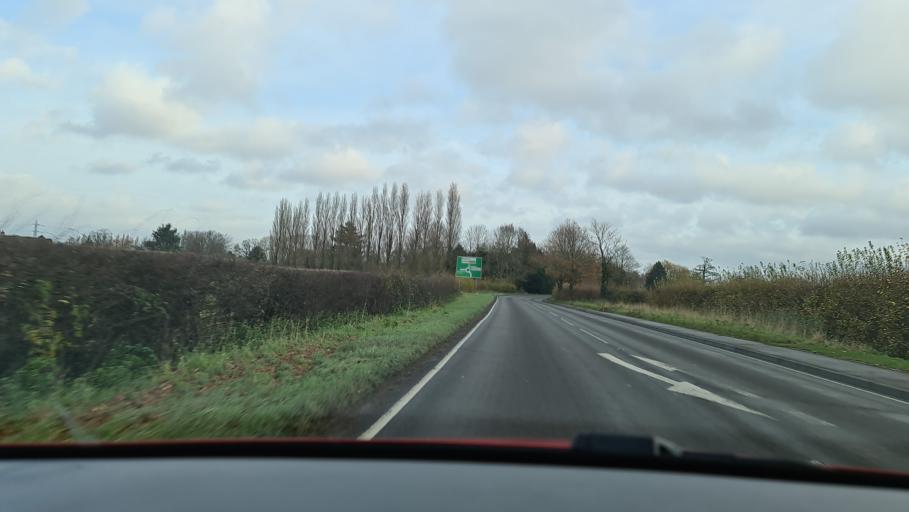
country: GB
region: England
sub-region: Buckinghamshire
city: Weston Turville
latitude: 51.7639
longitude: -0.7883
